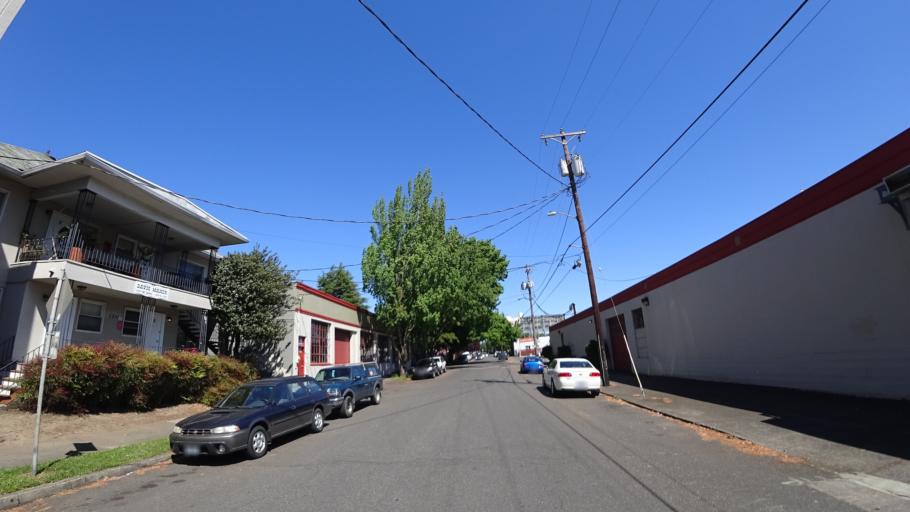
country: US
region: Oregon
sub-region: Multnomah County
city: Portland
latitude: 45.5243
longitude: -122.6523
